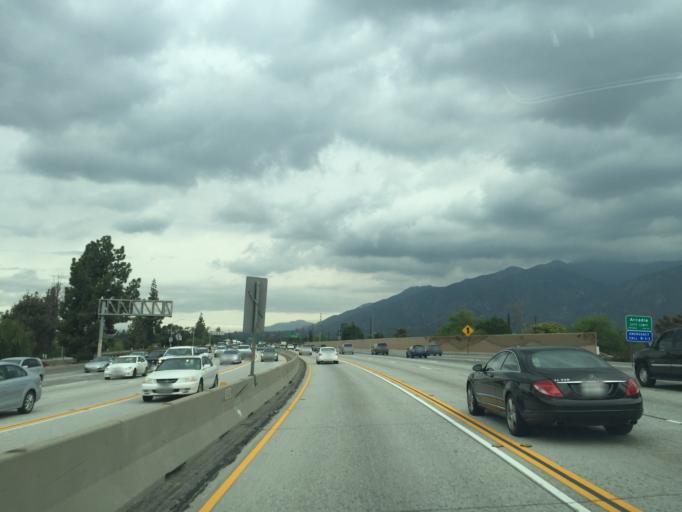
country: US
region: California
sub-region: Los Angeles County
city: Arcadia
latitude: 34.1414
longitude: -118.0178
